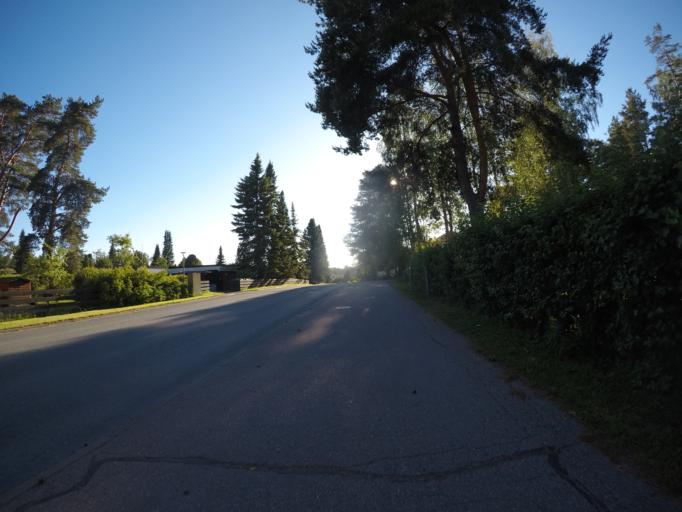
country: FI
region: Haeme
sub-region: Haemeenlinna
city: Haemeenlinna
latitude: 60.9829
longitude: 24.4500
